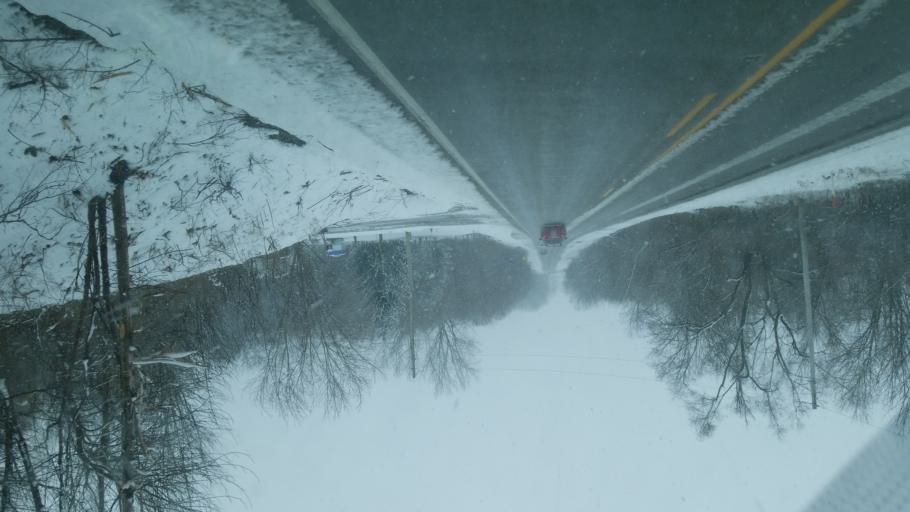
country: US
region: Indiana
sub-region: Wayne County
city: Hagerstown
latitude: 40.0105
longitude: -85.1676
